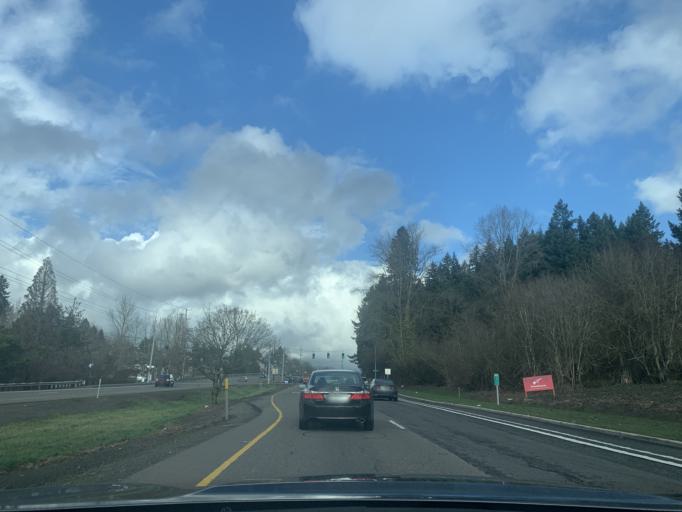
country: US
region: Oregon
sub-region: Washington County
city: King City
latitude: 45.4103
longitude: -122.7939
